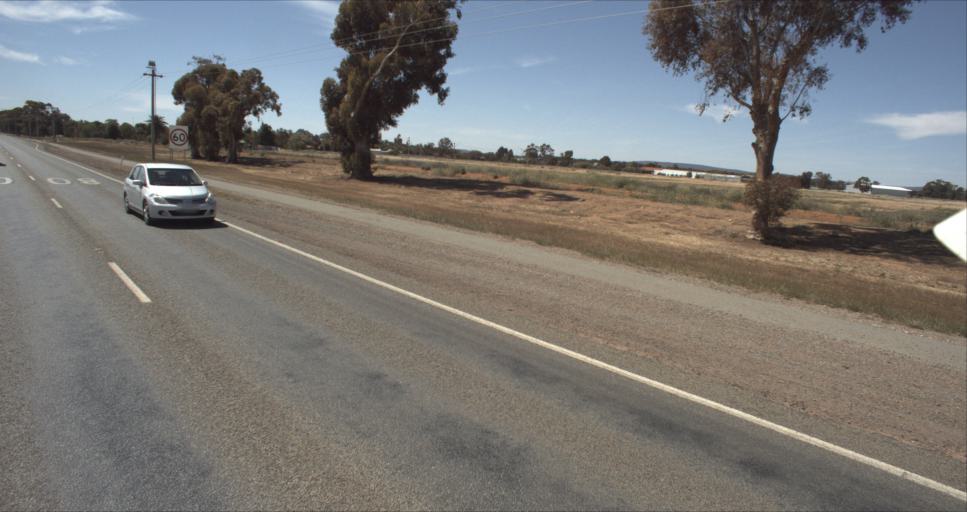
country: AU
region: New South Wales
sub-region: Leeton
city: Leeton
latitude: -34.5761
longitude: 146.4140
